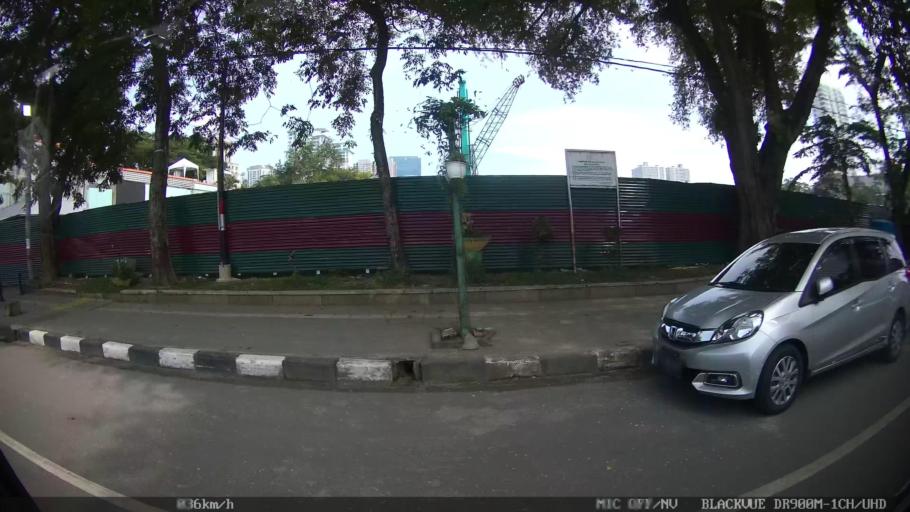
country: ID
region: North Sumatra
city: Medan
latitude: 3.5895
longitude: 98.6794
